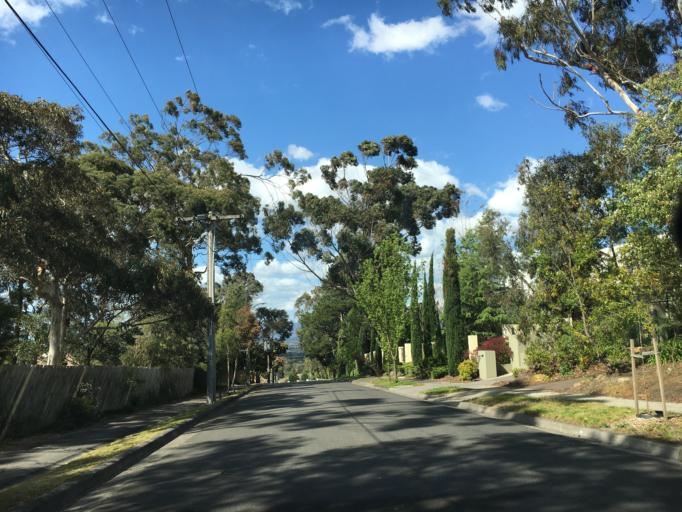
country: AU
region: Victoria
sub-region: Monash
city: Mulgrave
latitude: -37.8934
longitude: 145.1805
